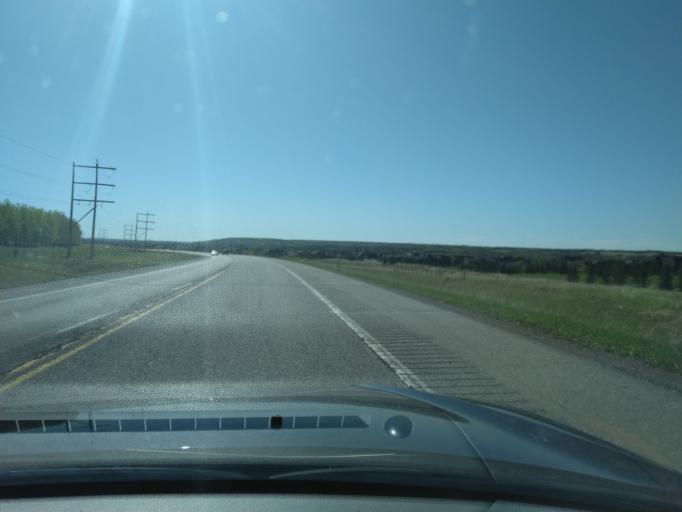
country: CA
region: Alberta
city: Cochrane
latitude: 51.0206
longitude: -114.3250
